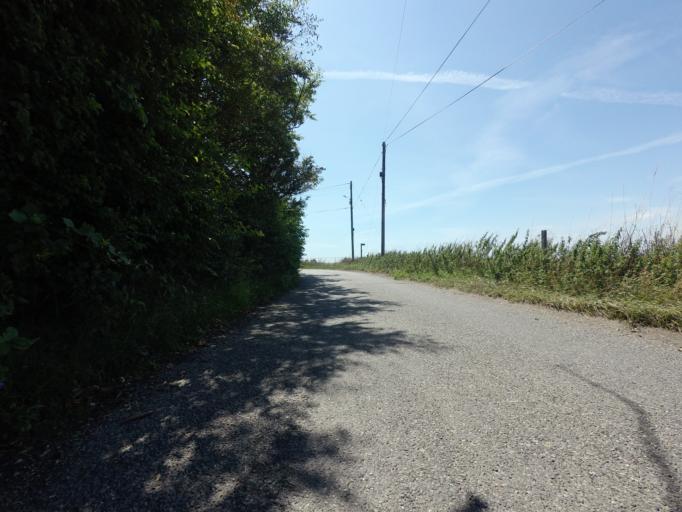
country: GB
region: England
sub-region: Kent
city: Lydd
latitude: 50.9592
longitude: 0.9030
